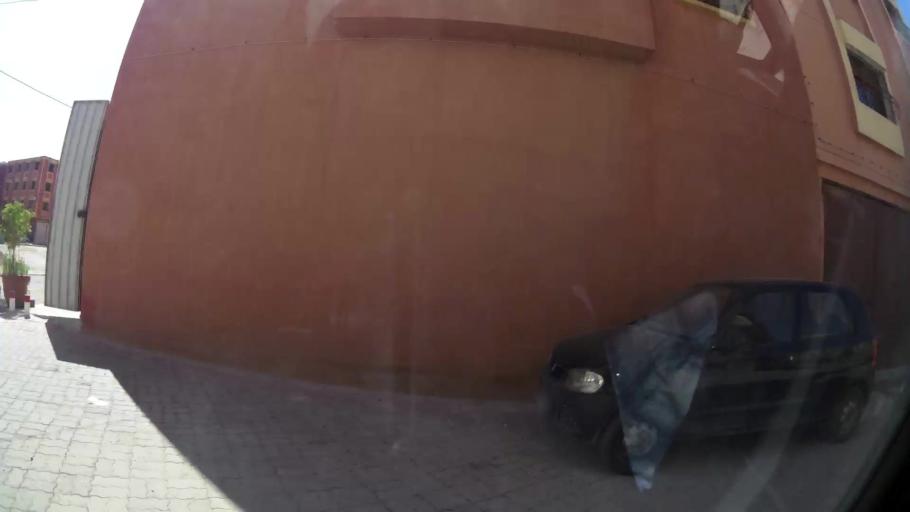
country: MA
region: Souss-Massa-Draa
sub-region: Inezgane-Ait Mellou
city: Inezgane
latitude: 30.3306
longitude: -9.5053
